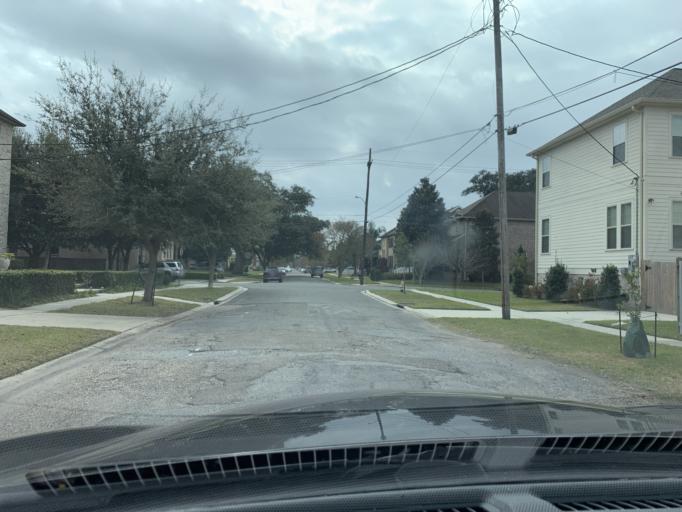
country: US
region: Louisiana
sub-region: Jefferson Parish
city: Metairie
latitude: 30.0179
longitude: -90.1042
